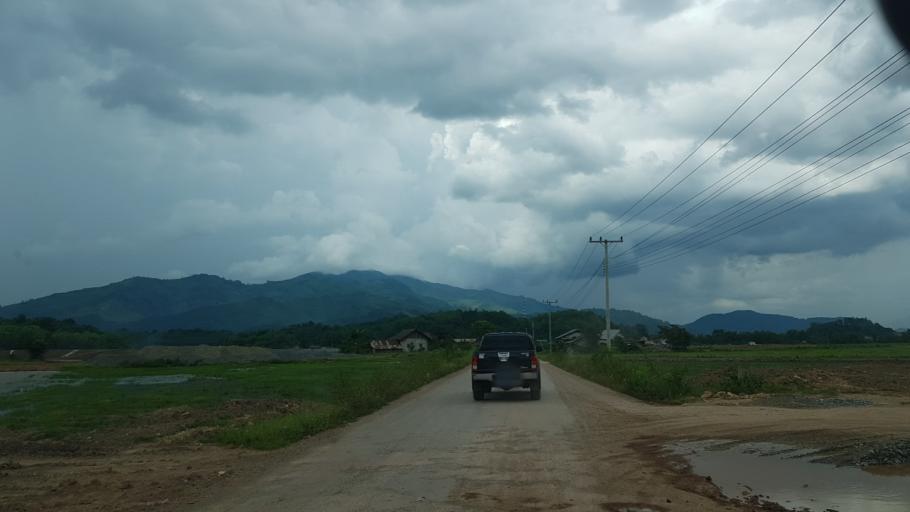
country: LA
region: Oudomxai
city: Muang Xay
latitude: 20.6766
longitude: 101.9698
